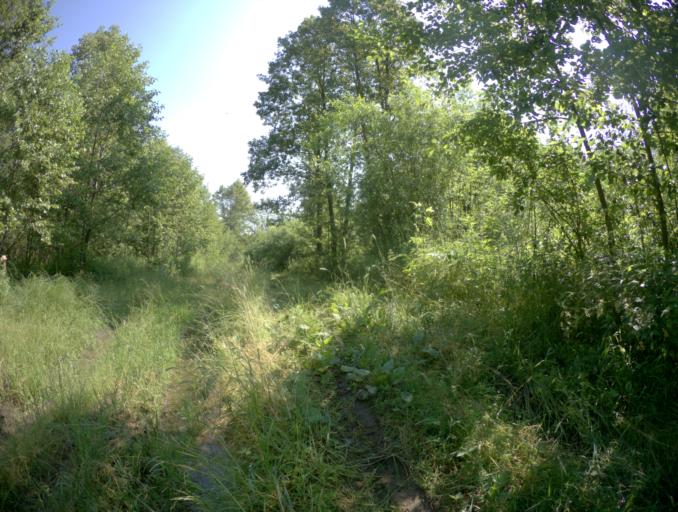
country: RU
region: Vladimir
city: Vyazniki
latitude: 56.3479
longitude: 42.1880
